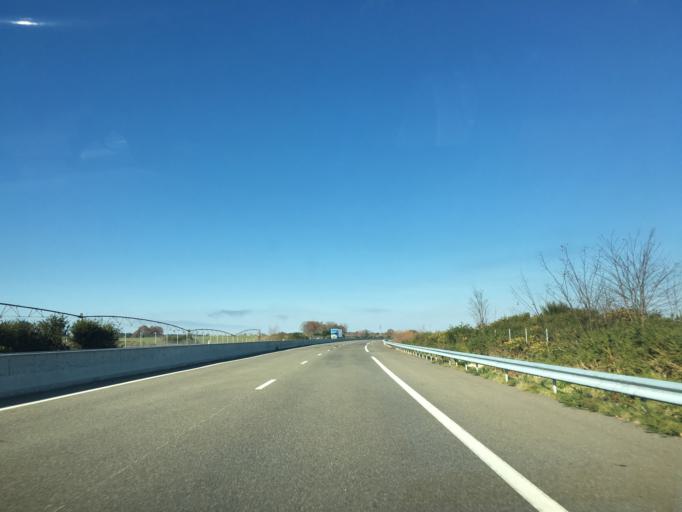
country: FR
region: Aquitaine
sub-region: Departement des Landes
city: Villeneuve-de-Marsan
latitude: 43.8591
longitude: -0.3521
